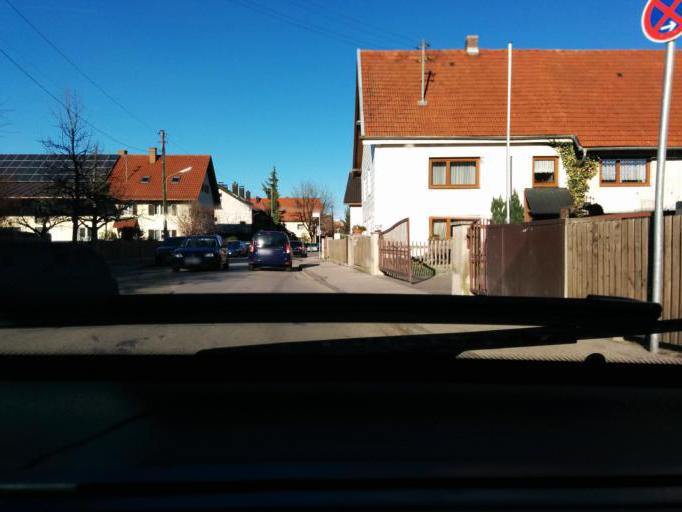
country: DE
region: Bavaria
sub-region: Upper Bavaria
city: Germering
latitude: 48.1607
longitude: 11.4127
